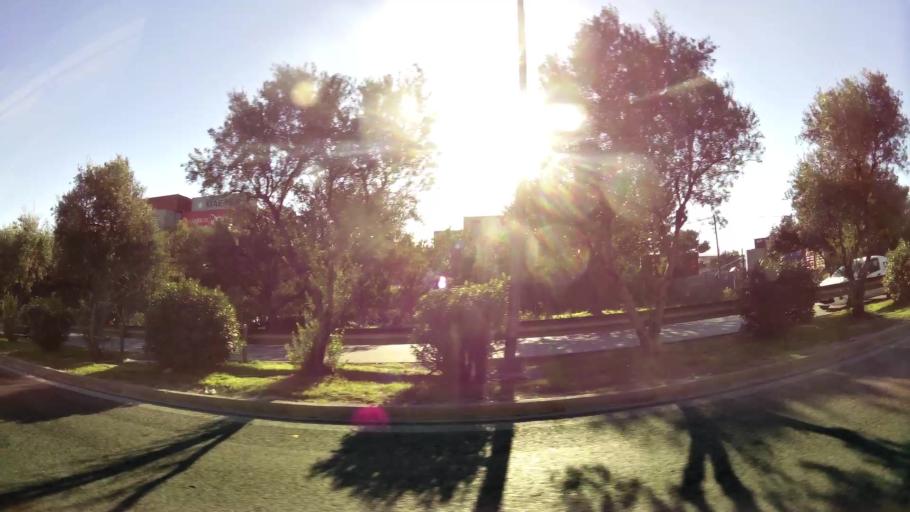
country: GR
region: Attica
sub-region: Nomos Piraios
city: Perama
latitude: 37.9798
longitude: 23.5960
